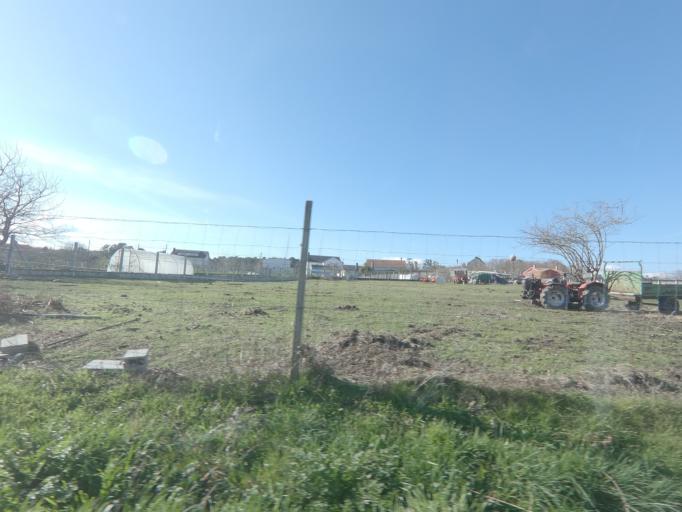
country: ES
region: Galicia
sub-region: Provincia da Coruna
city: Ribeira
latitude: 42.7106
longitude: -8.4451
